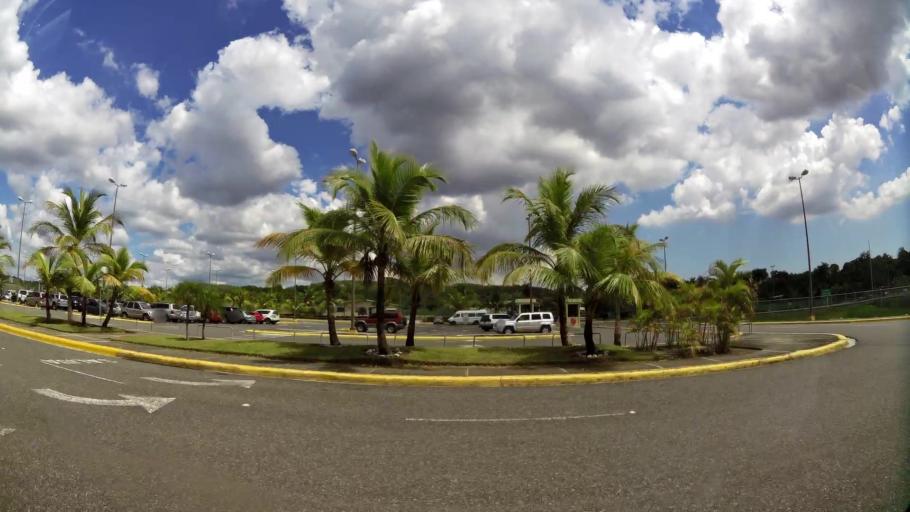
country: DO
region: Nacional
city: Santo Domingo
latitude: 18.5752
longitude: -69.9815
